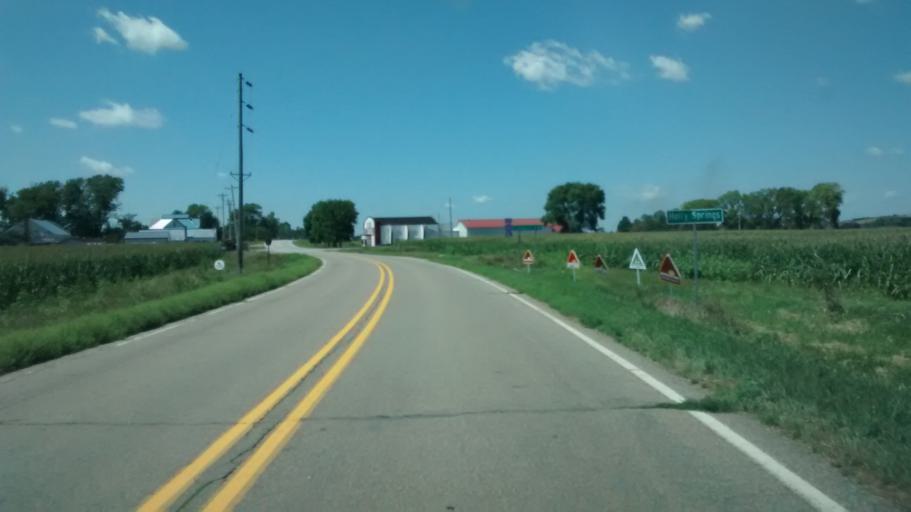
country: US
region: Iowa
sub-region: Woodbury County
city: Moville
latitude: 42.2706
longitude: -96.0751
